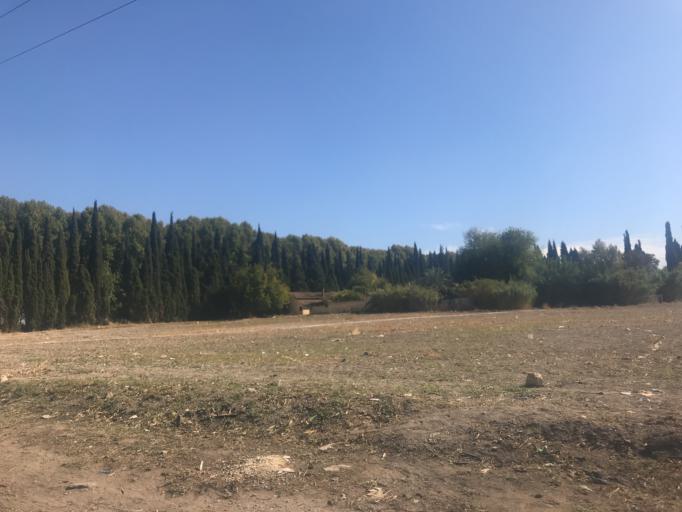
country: MA
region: Fes-Boulemane
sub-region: Fes
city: Fes
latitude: 34.0041
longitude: -5.0350
